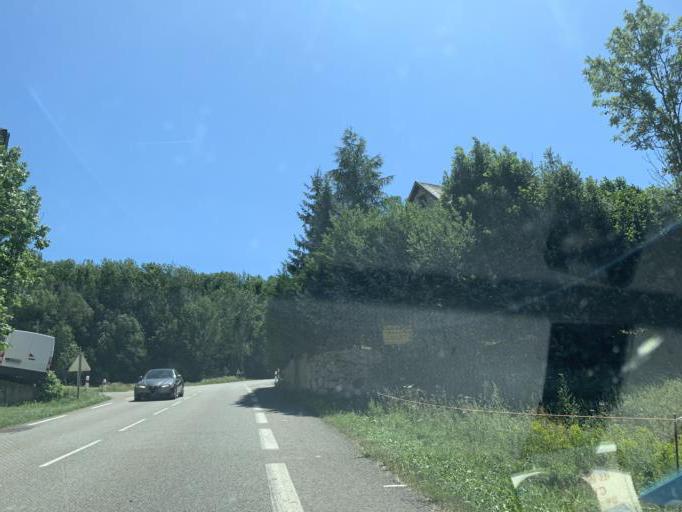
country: FR
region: Provence-Alpes-Cote d'Azur
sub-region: Departement des Hautes-Alpes
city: Saint-Bonnet-en-Champsaur
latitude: 44.6339
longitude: 6.1366
